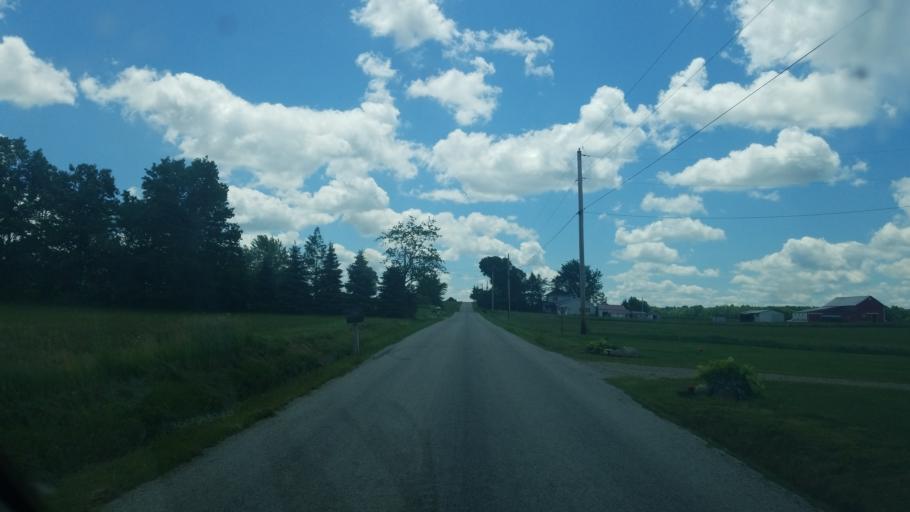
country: US
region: Ohio
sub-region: Huron County
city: New London
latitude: 41.0013
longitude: -82.3254
